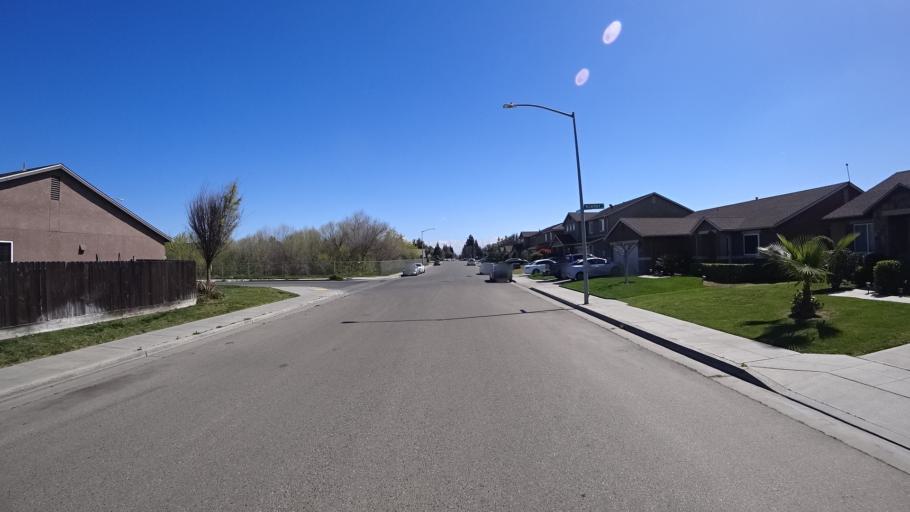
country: US
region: California
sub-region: Fresno County
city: West Park
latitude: 36.7830
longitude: -119.8914
